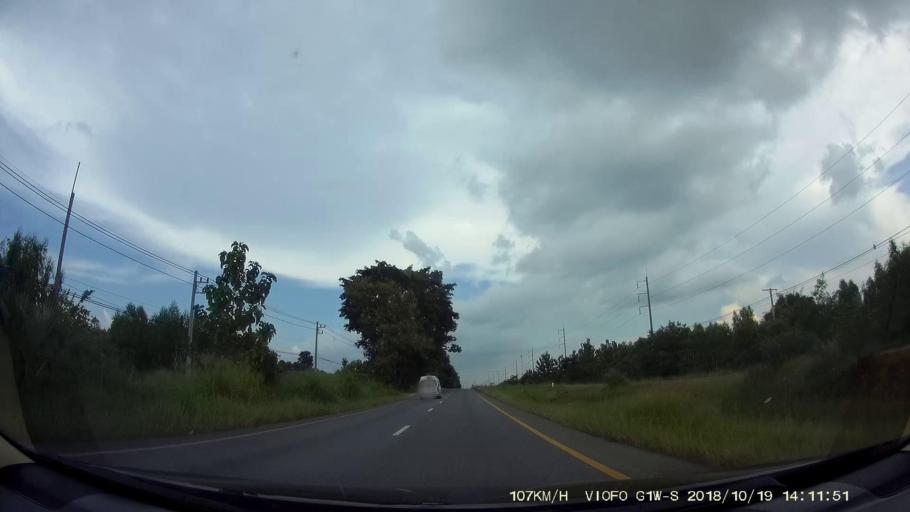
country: TH
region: Chaiyaphum
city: Khon Sawan
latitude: 15.9426
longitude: 102.1659
